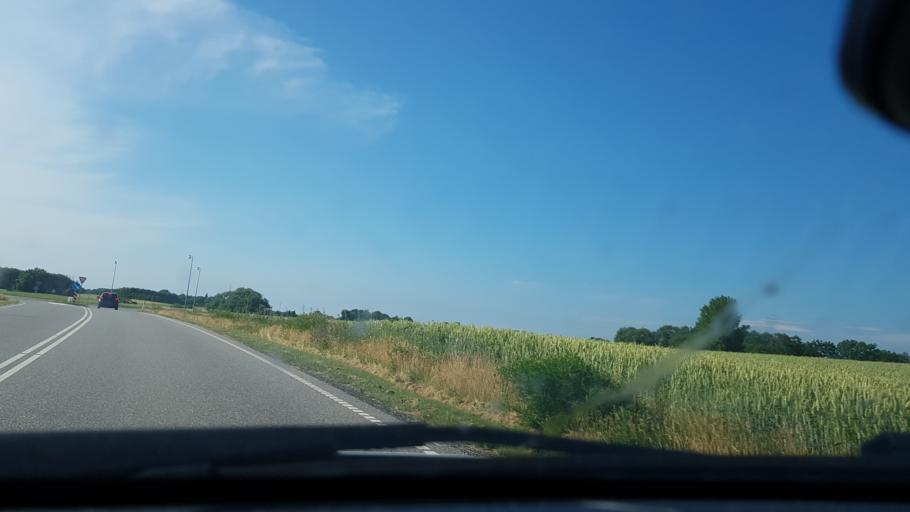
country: DK
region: Zealand
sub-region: Odsherred Kommune
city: Hojby
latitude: 55.8560
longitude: 11.5919
